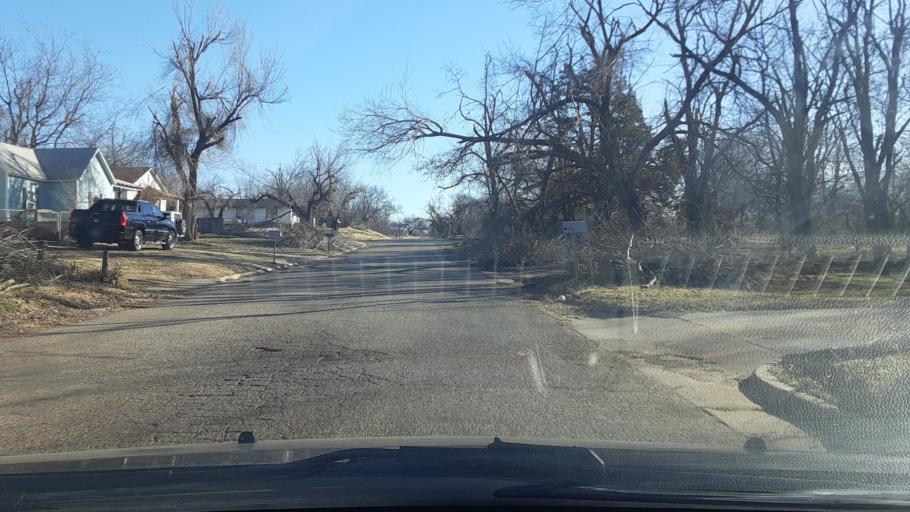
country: US
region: Oklahoma
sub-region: Logan County
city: Guthrie
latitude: 35.8728
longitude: -97.4185
